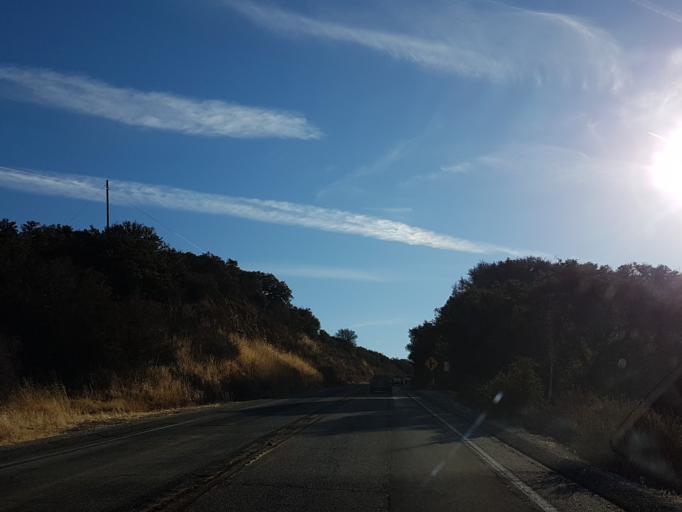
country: US
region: California
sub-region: Santa Barbara County
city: Santa Ynez
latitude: 34.5679
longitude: -119.9463
